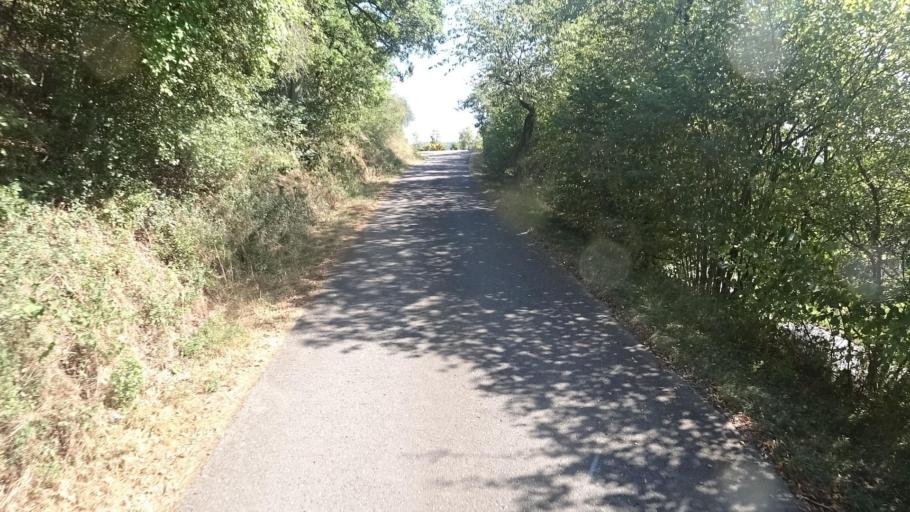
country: DE
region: Rheinland-Pfalz
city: Mengerschied
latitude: 49.9149
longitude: 7.5048
